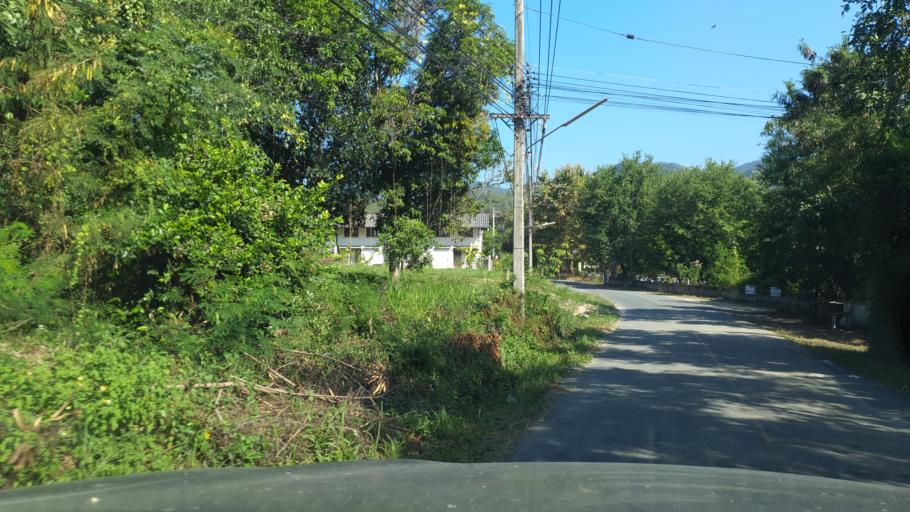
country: TH
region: Chiang Mai
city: San Sai
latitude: 18.8859
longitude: 99.1649
